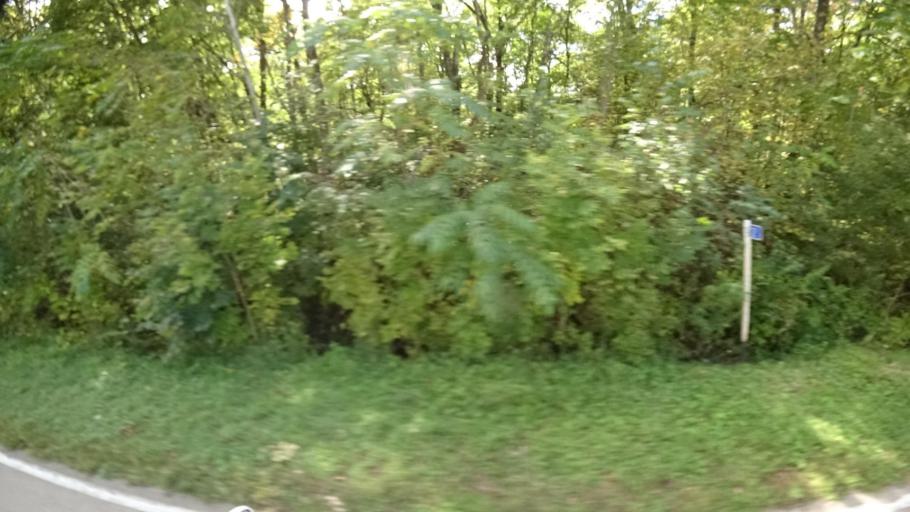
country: RU
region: Primorskiy
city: Yakovlevka
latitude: 44.4047
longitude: 133.5935
